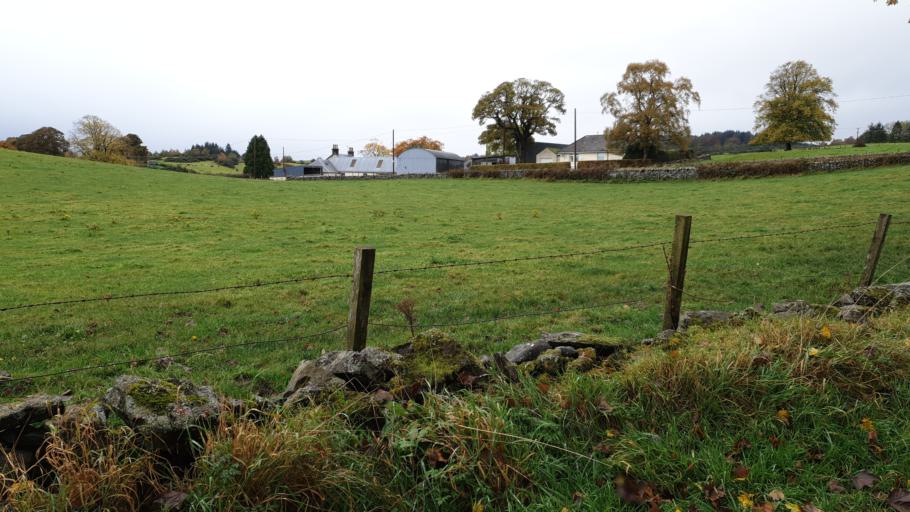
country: GB
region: Scotland
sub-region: Renfrewshire
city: Houston
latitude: 55.8892
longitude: -4.5514
